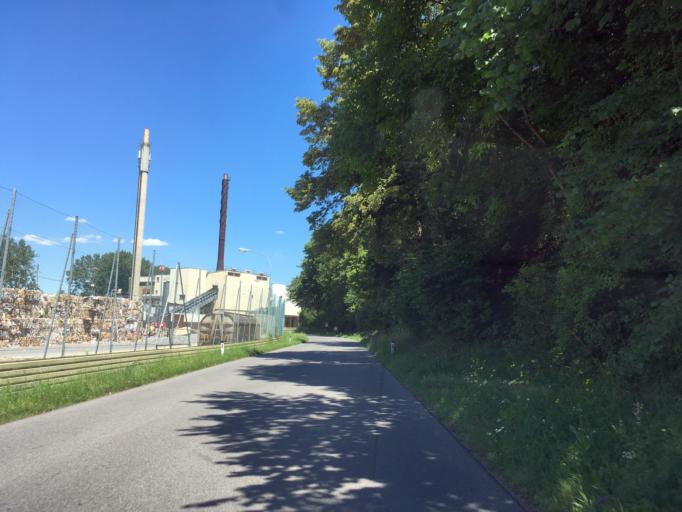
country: AT
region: Lower Austria
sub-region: Politischer Bezirk Neunkirchen
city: Pitten
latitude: 47.7040
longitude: 16.1726
